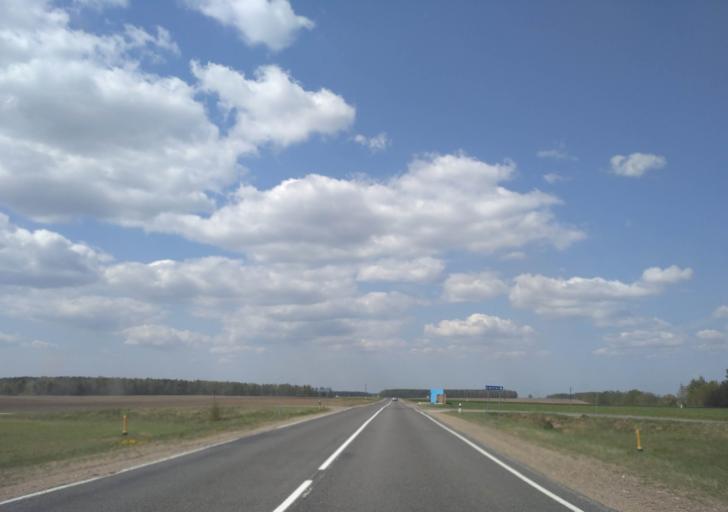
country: BY
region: Minsk
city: Vilyeyka
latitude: 54.5132
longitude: 27.0467
